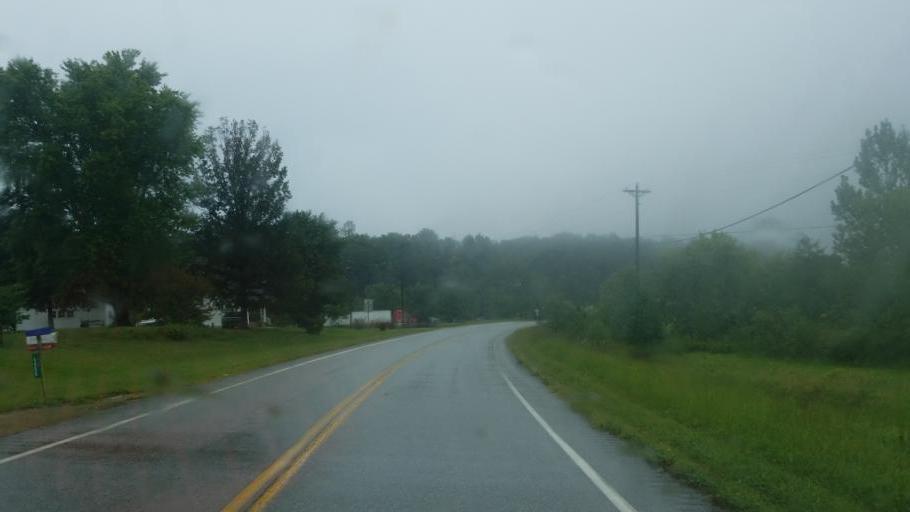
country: US
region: Kentucky
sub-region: Greenup County
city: South Shore
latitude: 38.6767
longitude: -82.9255
